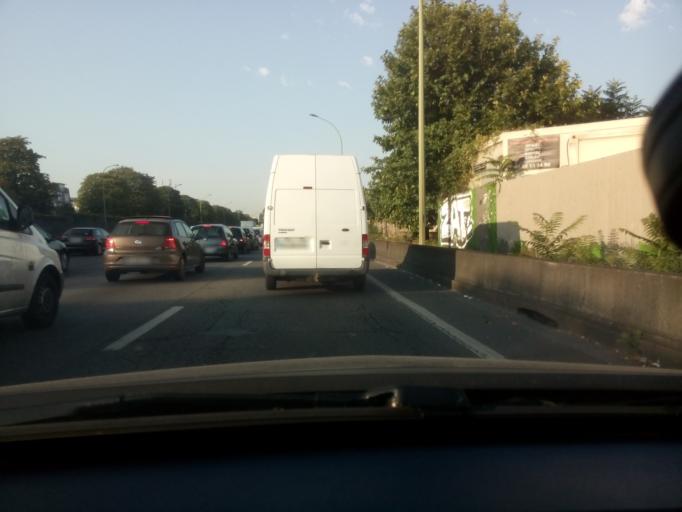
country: FR
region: Ile-de-France
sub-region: Departement du Val-de-Marne
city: Saint-Mande
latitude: 48.8383
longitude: 2.4128
